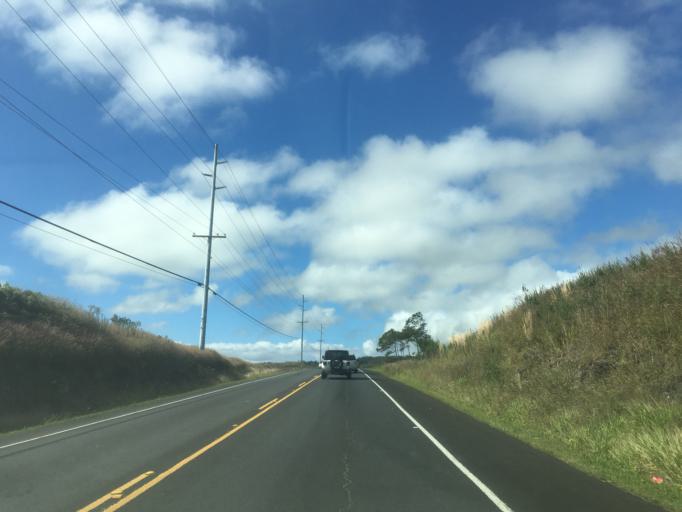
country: US
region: Hawaii
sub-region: Hawaii County
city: Waimea
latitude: 20.0476
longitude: -155.5793
